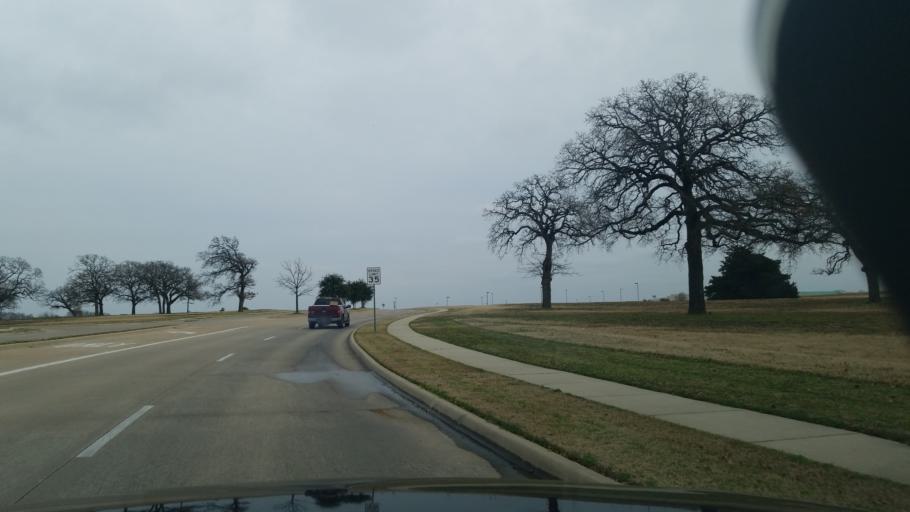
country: US
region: Texas
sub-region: Denton County
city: Corinth
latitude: 33.1443
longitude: -97.0468
